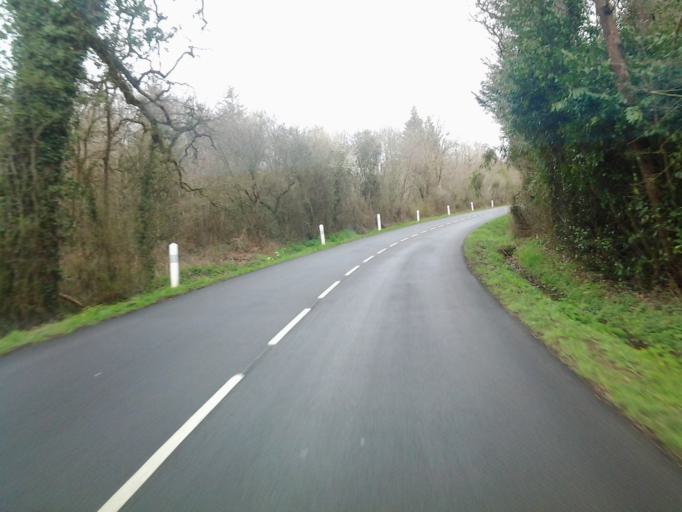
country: FR
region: Pays de la Loire
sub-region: Departement de la Vendee
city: Avrille
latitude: 46.4873
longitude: -1.4668
